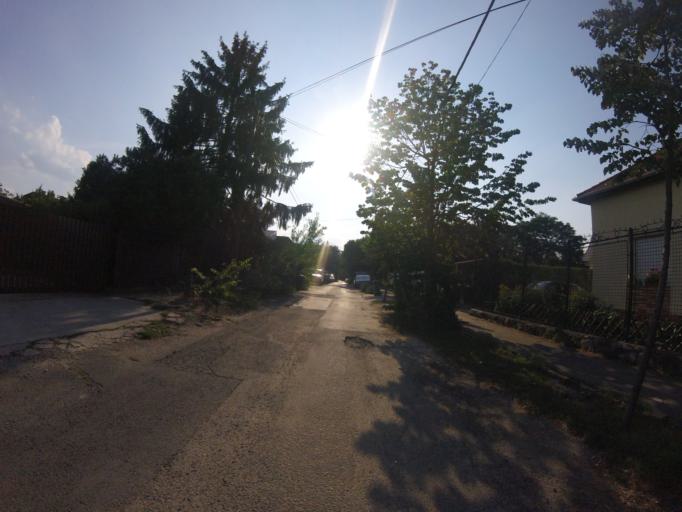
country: HU
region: Pest
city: Budakalasz
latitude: 47.5880
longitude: 19.0540
